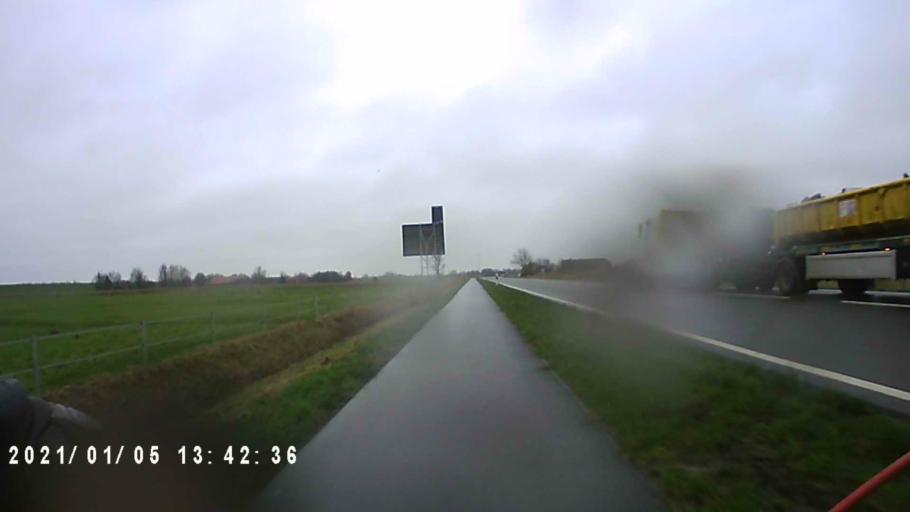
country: DE
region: Lower Saxony
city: Weener
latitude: 53.1986
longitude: 7.3989
